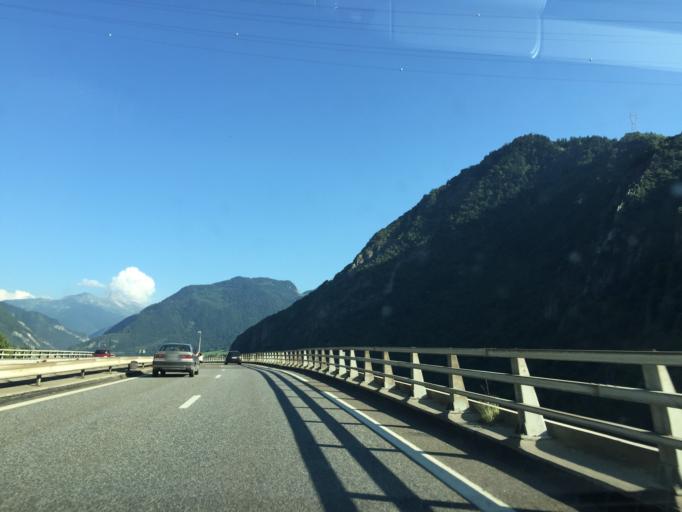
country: FR
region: Rhone-Alpes
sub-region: Departement de la Savoie
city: Aigueblanche
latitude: 45.5328
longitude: 6.4746
